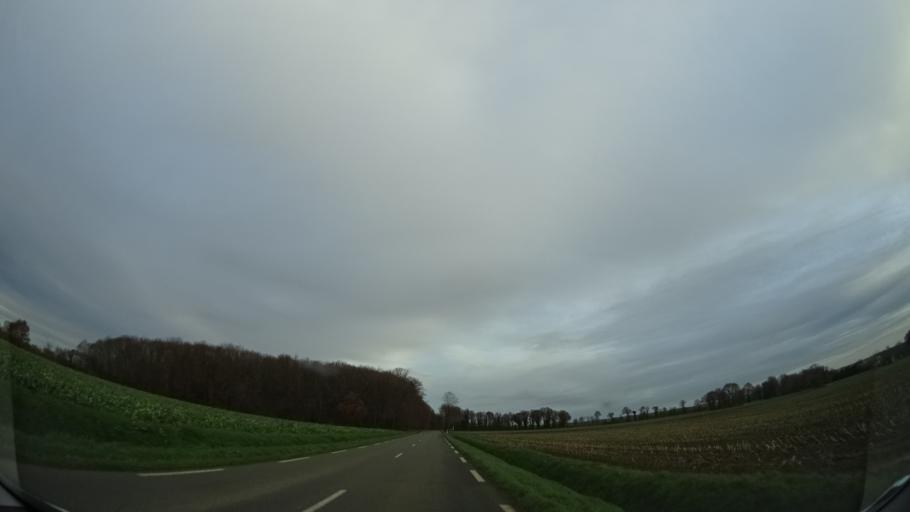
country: FR
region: Brittany
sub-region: Departement des Cotes-d'Armor
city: Evran
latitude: 48.3511
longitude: -1.9693
